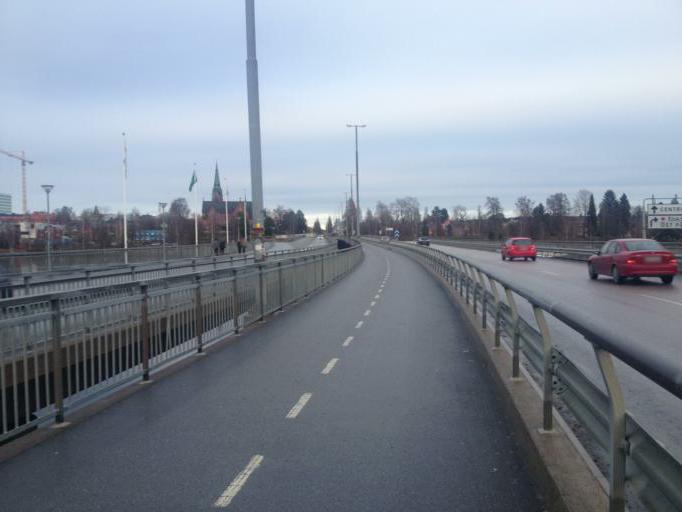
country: SE
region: Vaesterbotten
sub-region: Umea Kommun
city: Umea
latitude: 63.8199
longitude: 20.2660
